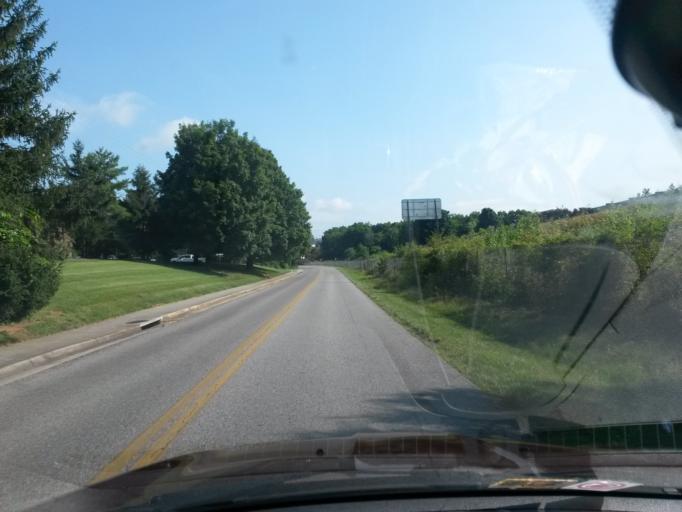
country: US
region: Virginia
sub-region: Roanoke County
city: Hollins
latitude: 37.3085
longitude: -79.9766
